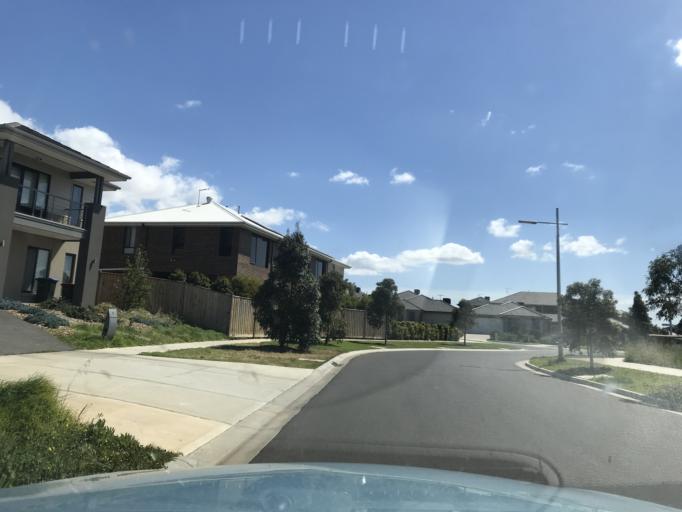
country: AU
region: Victoria
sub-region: Wyndham
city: Williams Landing
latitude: -37.8625
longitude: 144.7372
